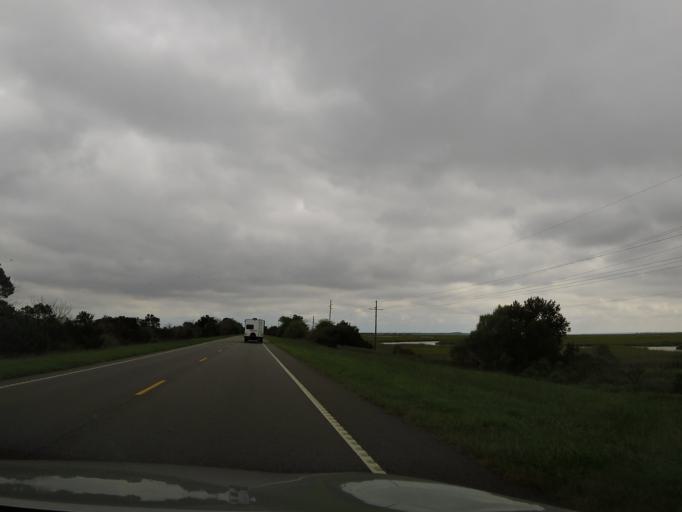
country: US
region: Georgia
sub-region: Glynn County
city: Brunswick
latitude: 31.0664
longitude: -81.4567
